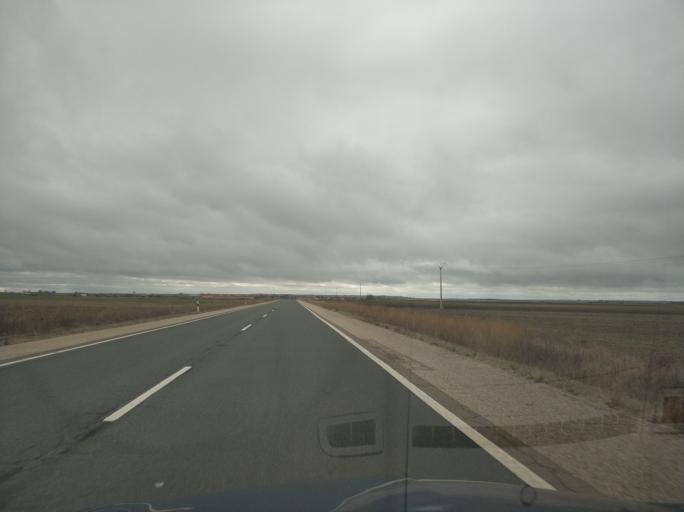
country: ES
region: Castille and Leon
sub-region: Provincia de Salamanca
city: Villaverde de Guarena
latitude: 41.0748
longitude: -5.5289
